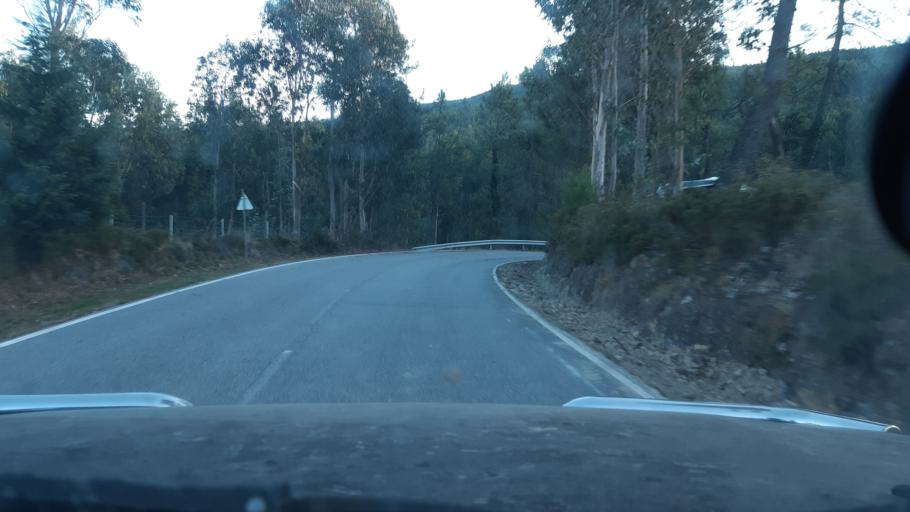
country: PT
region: Viseu
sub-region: Mortagua
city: Mortagua
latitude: 40.5440
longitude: -8.2640
